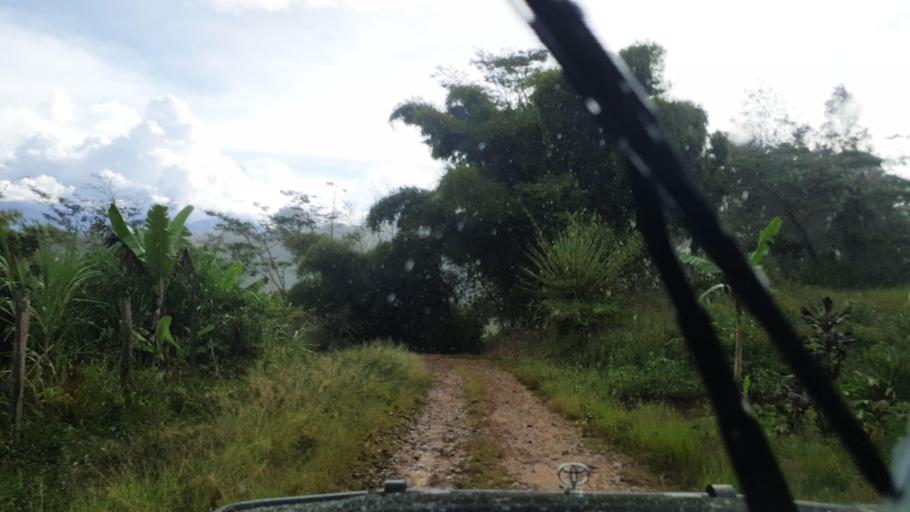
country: PG
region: Jiwaka
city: Minj
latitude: -5.8897
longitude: 144.8183
